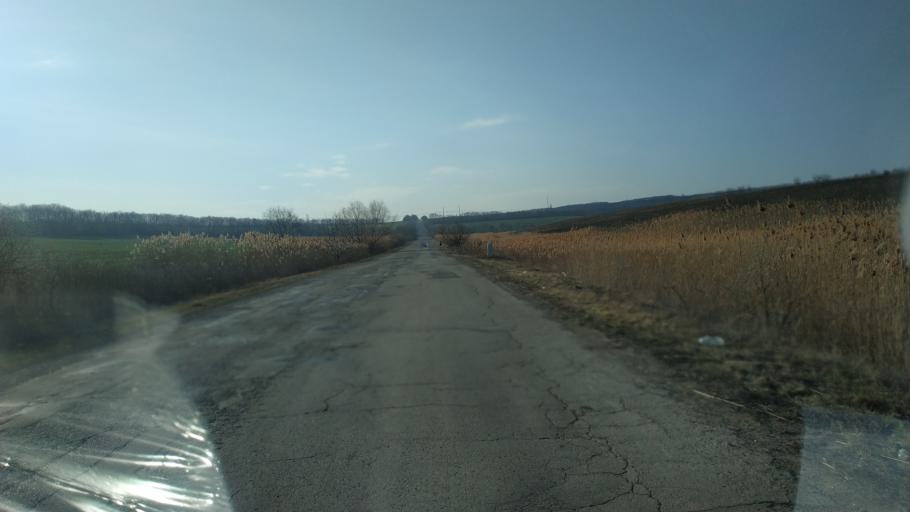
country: MD
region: Chisinau
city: Singera
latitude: 46.8838
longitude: 29.0393
